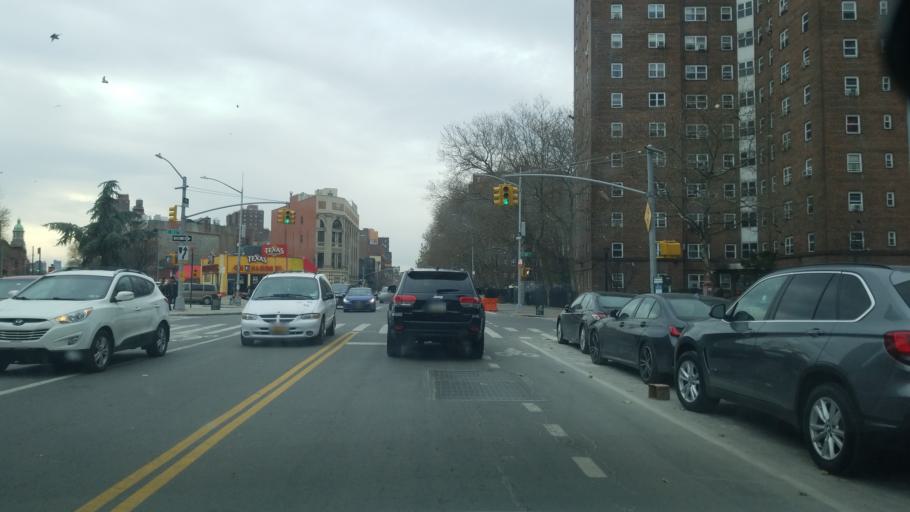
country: US
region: New York
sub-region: New York County
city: Inwood
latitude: 40.8135
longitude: -73.9226
